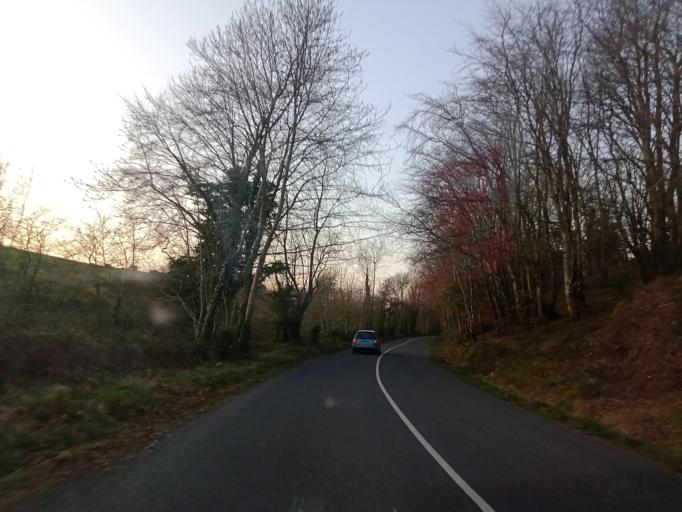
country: IE
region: Leinster
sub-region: Kilkenny
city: Castlecomer
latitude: 52.8419
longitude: -7.2584
